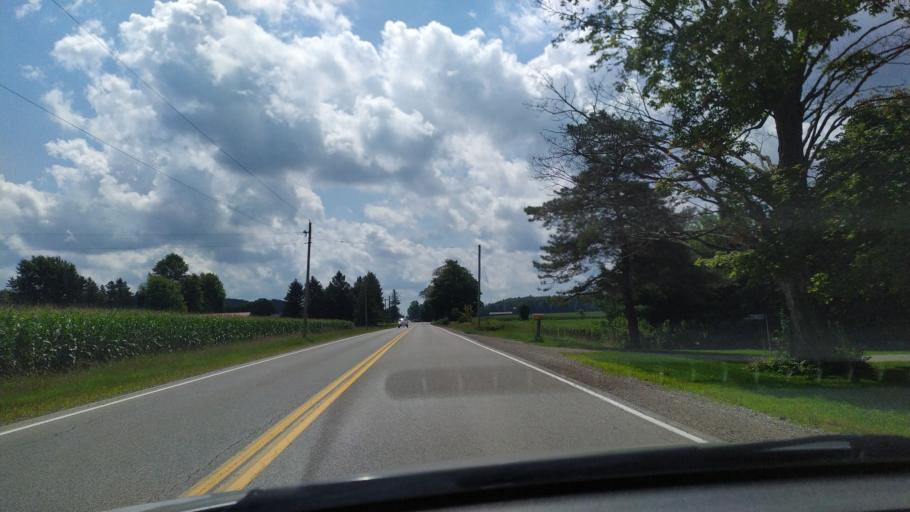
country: CA
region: Ontario
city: London
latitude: 43.0561
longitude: -81.3302
